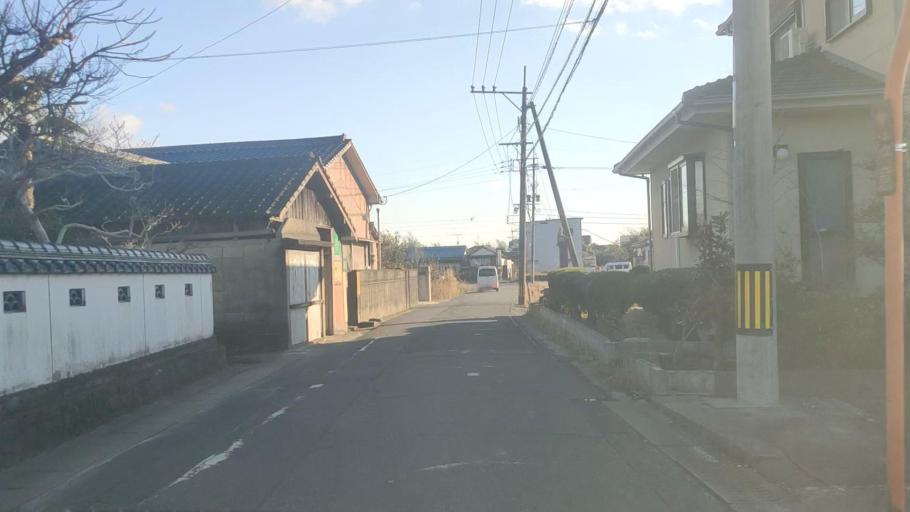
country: JP
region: Saga Prefecture
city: Saga-shi
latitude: 33.2931
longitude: 130.2404
